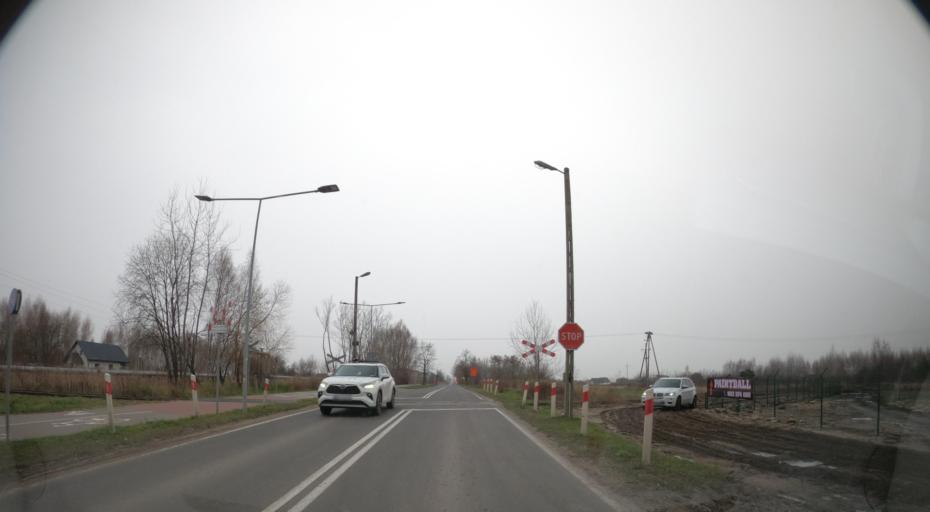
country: PL
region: Masovian Voivodeship
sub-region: Radom
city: Radom
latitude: 51.4414
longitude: 21.1895
